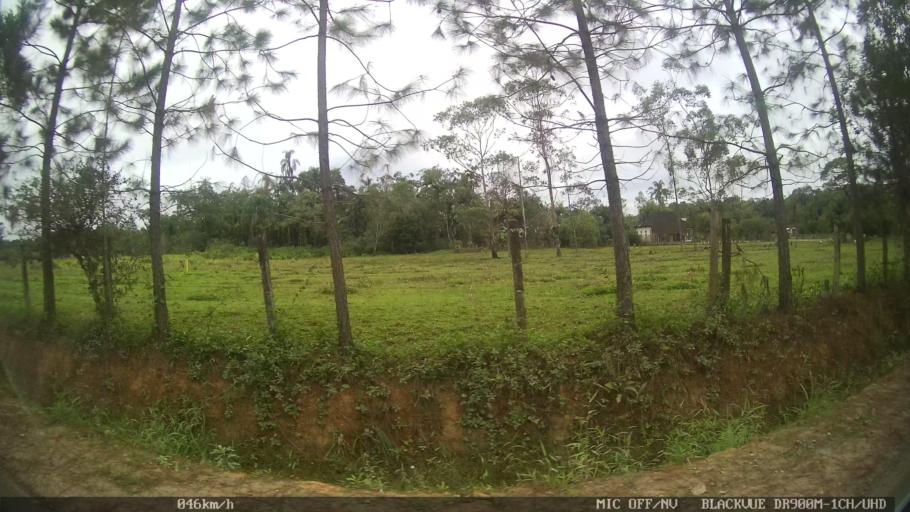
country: BR
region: Santa Catarina
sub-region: Joinville
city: Joinville
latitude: -26.2674
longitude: -48.9321
